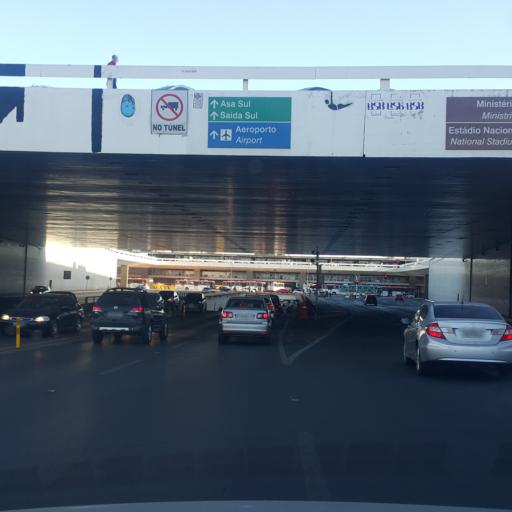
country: BR
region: Federal District
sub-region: Brasilia
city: Brasilia
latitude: -15.7911
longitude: -47.8819
